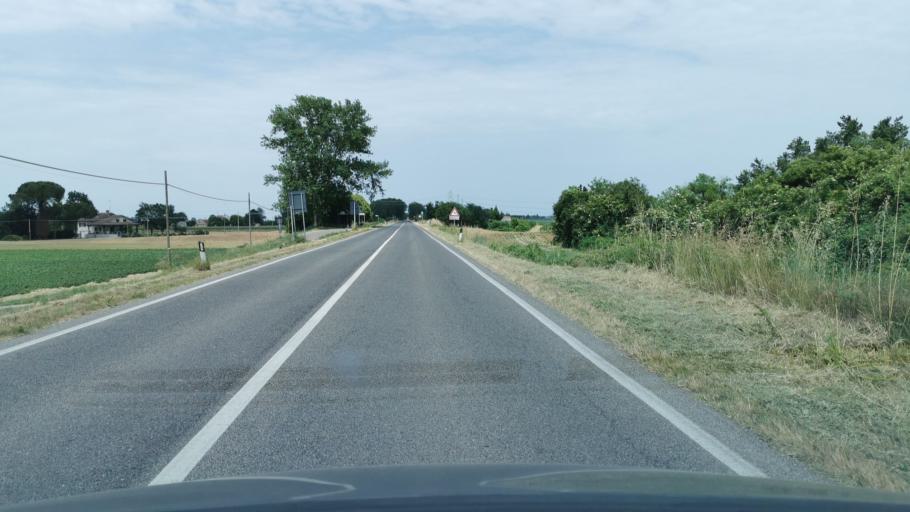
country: IT
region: Emilia-Romagna
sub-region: Provincia di Ravenna
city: Savarna-Conventella
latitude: 44.5188
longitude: 12.1067
